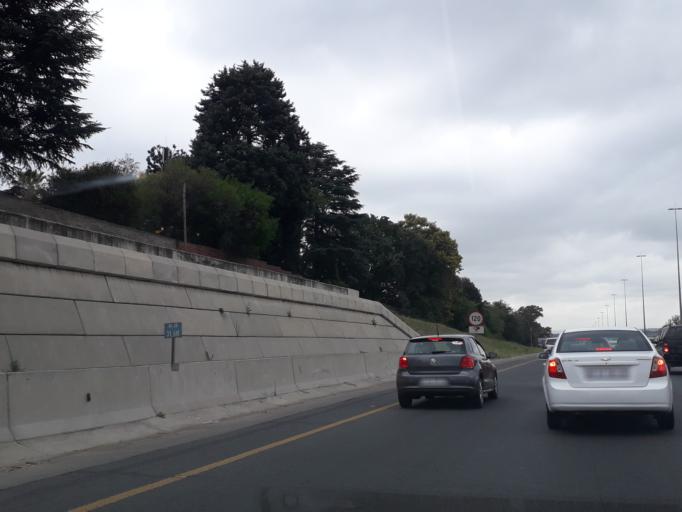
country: ZA
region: Gauteng
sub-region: City of Johannesburg Metropolitan Municipality
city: Roodepoort
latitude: -26.1081
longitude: 27.9591
